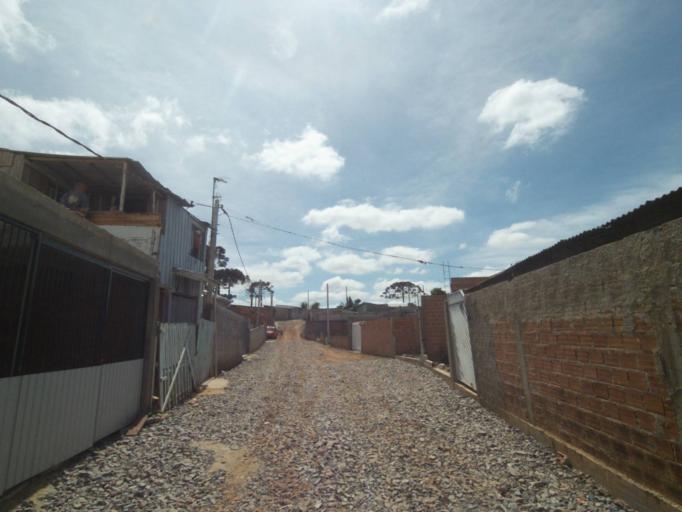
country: BR
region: Parana
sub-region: Curitiba
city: Curitiba
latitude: -25.4916
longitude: -49.3392
